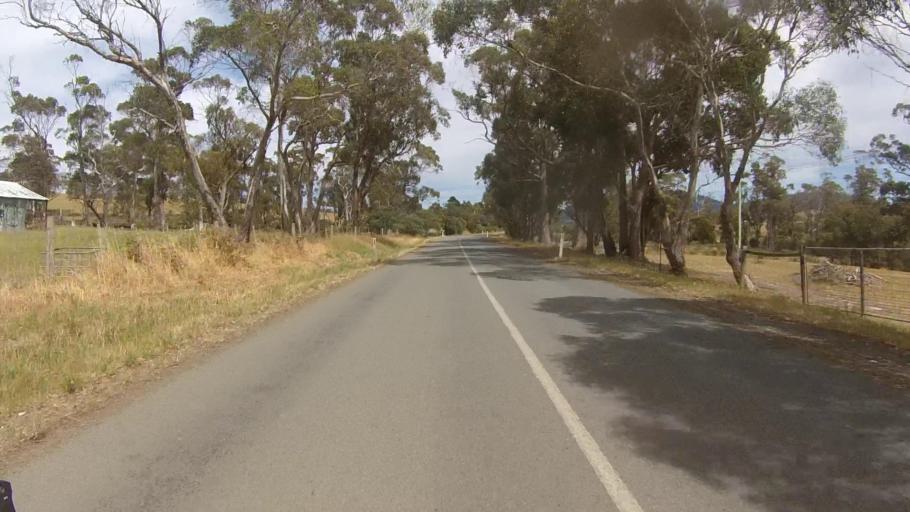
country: AU
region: Tasmania
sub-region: Sorell
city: Sorell
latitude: -42.8193
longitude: 147.8124
